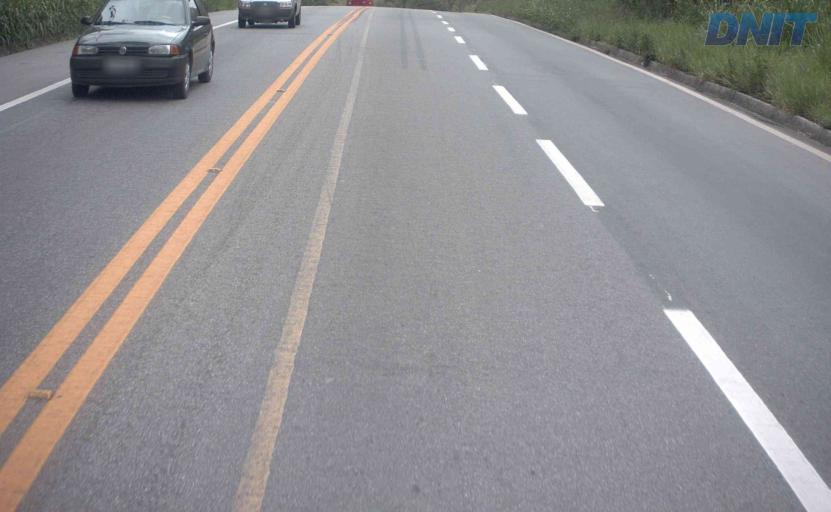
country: BR
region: Minas Gerais
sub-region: Timoteo
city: Timoteo
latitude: -19.6313
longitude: -42.8332
